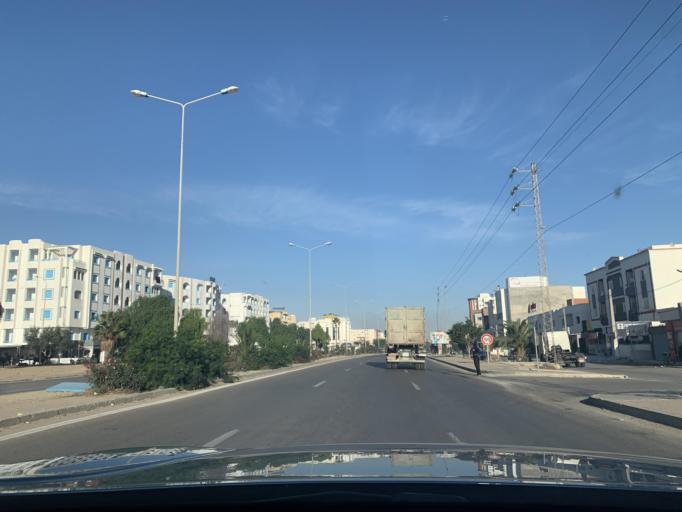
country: DZ
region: Souk Ahras
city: Souk Ahras
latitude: 36.3701
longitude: 7.9975
